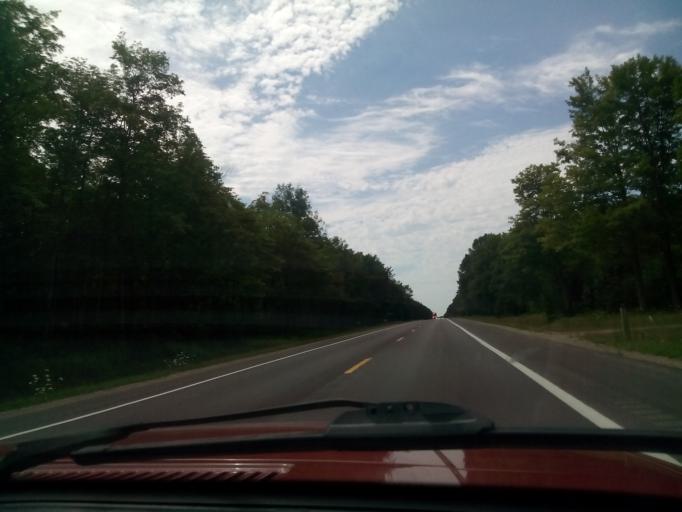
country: US
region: Michigan
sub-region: Schoolcraft County
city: Manistique
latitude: 46.0556
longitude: -85.9614
